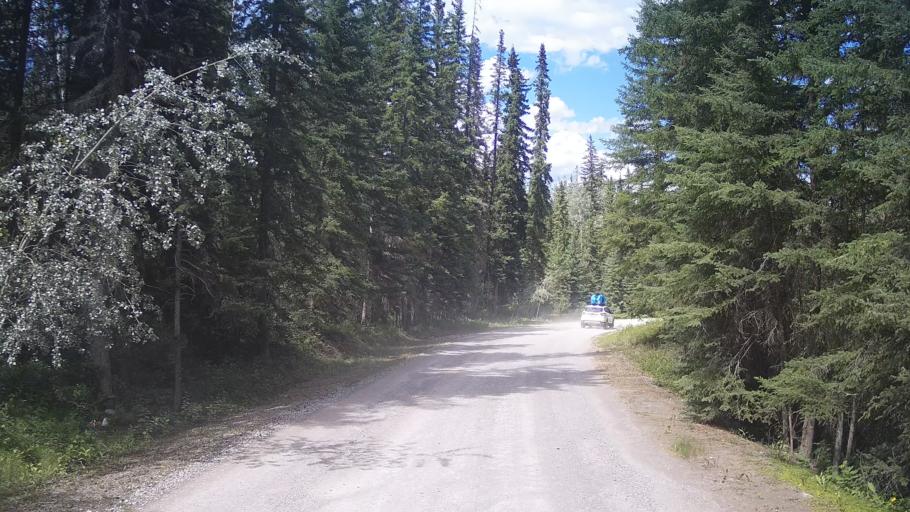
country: CA
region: British Columbia
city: Lillooet
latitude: 51.3134
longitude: -121.8257
